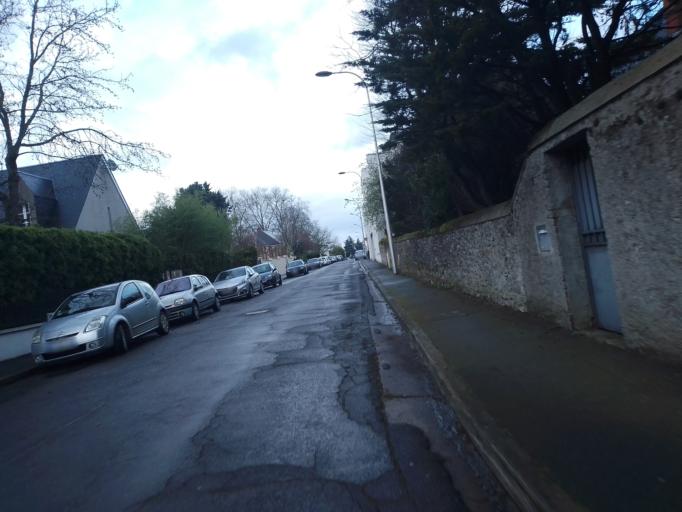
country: FR
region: Centre
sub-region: Departement du Loir-et-Cher
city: Blois
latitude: 47.5967
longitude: 1.3468
